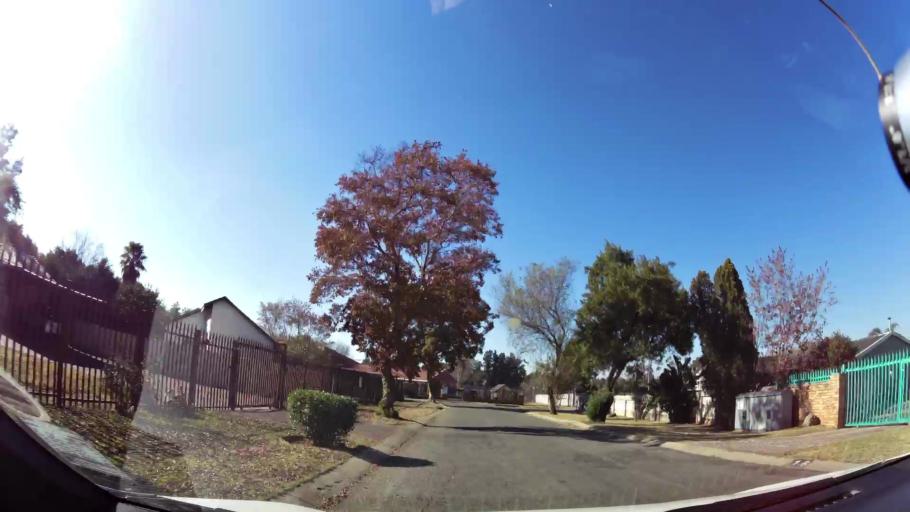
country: ZA
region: Gauteng
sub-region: Ekurhuleni Metropolitan Municipality
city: Germiston
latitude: -26.3303
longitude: 28.1087
